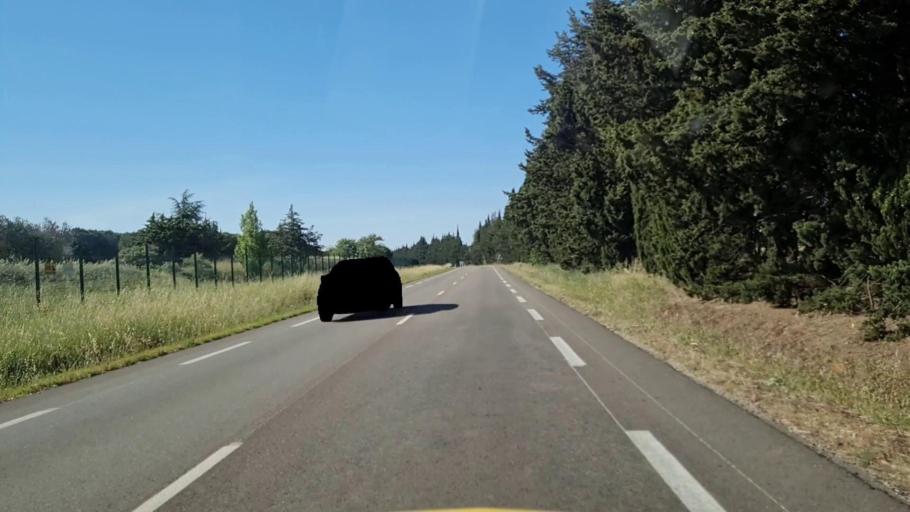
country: FR
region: Languedoc-Roussillon
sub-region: Departement du Gard
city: Garons
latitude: 43.7550
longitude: 4.4063
